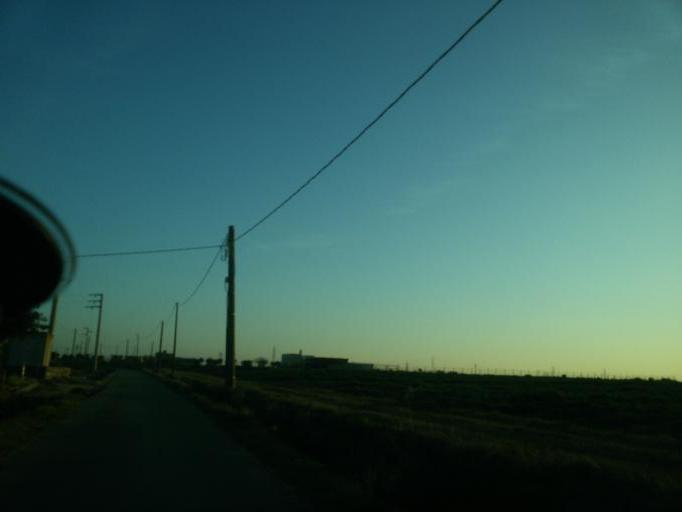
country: IT
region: Apulia
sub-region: Provincia di Brindisi
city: La Rosa
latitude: 40.6079
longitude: 17.9381
